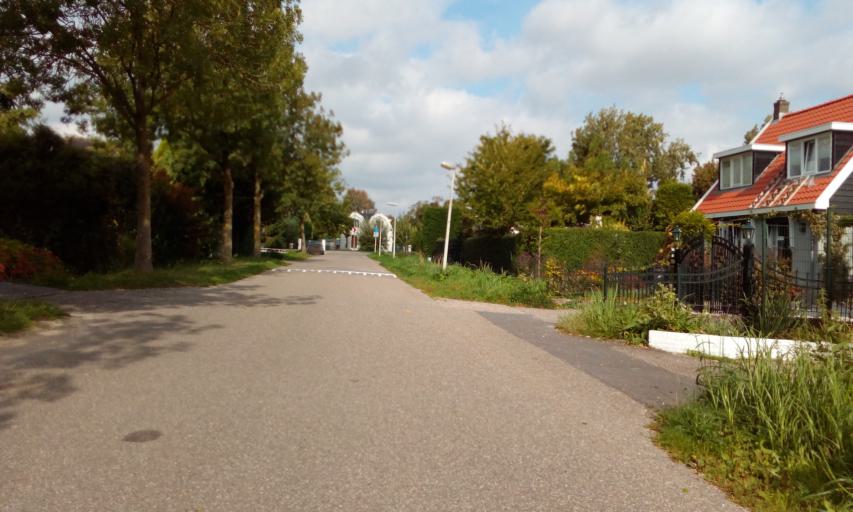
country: NL
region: South Holland
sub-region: Gemeente Rotterdam
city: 's-Gravenland
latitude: 51.9275
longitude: 4.5411
